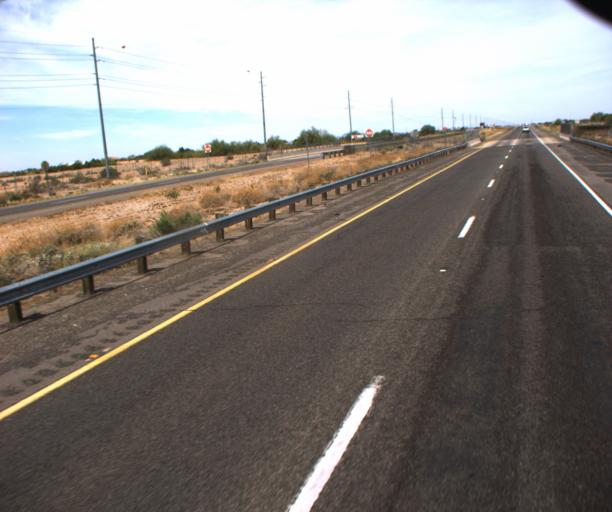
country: US
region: Arizona
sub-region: Maricopa County
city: Sun City West
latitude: 33.7450
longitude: -112.4862
